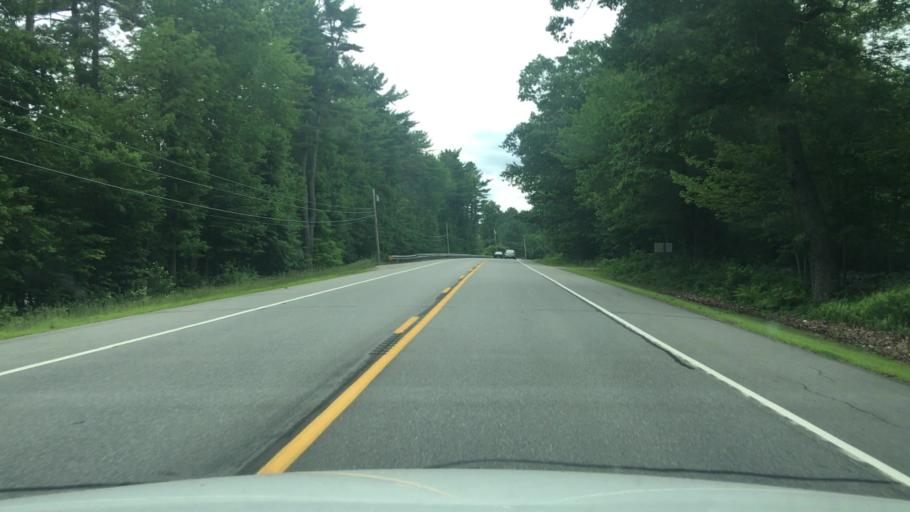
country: US
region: Maine
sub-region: Kennebec County
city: Windsor
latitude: 44.3540
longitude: -69.6451
